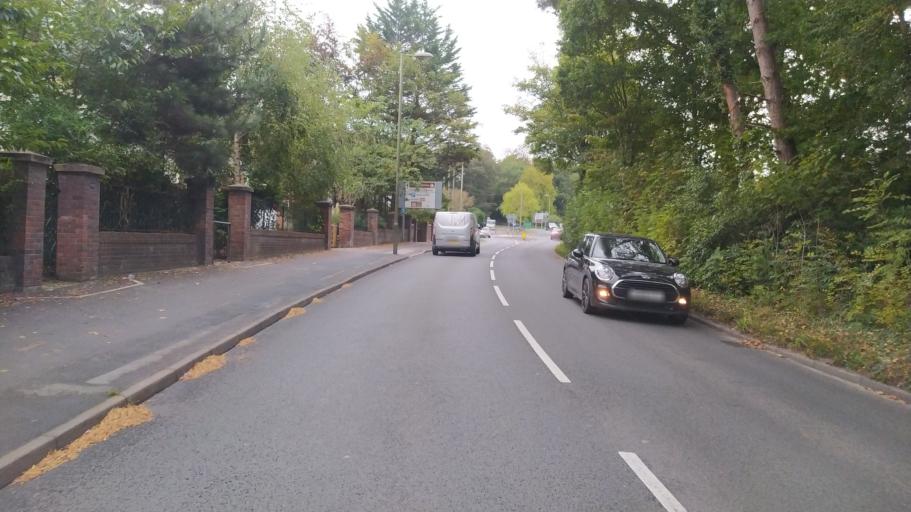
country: GB
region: England
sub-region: Hampshire
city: Lymington
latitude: 50.7696
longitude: -1.5519
